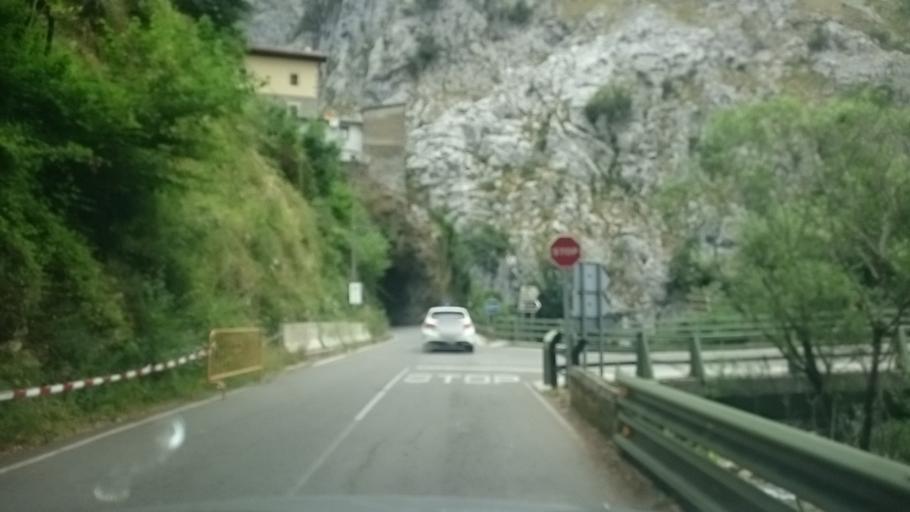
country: ES
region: Asturias
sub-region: Province of Asturias
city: Carrena
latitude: 43.2580
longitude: -4.8310
